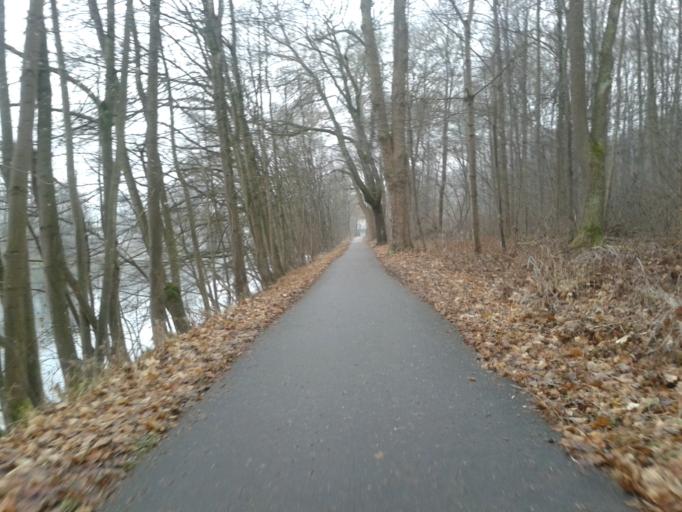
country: DE
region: Bavaria
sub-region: Swabia
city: Neu-Ulm
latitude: 48.4257
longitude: 10.0294
